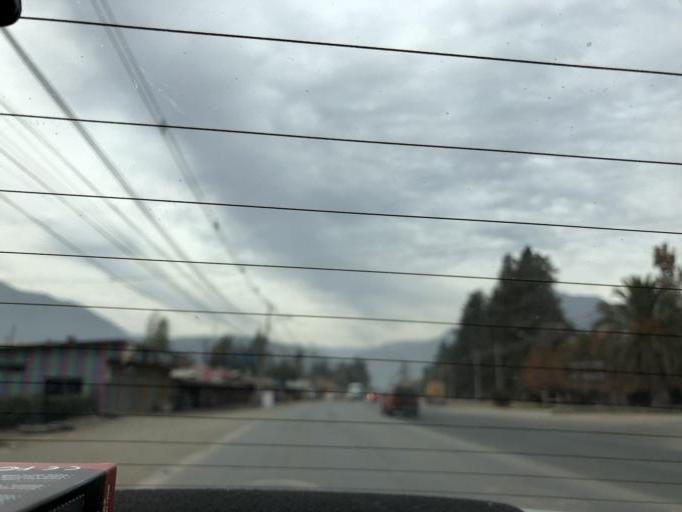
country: CL
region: Santiago Metropolitan
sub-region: Provincia de Cordillera
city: Puente Alto
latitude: -33.5983
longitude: -70.5255
